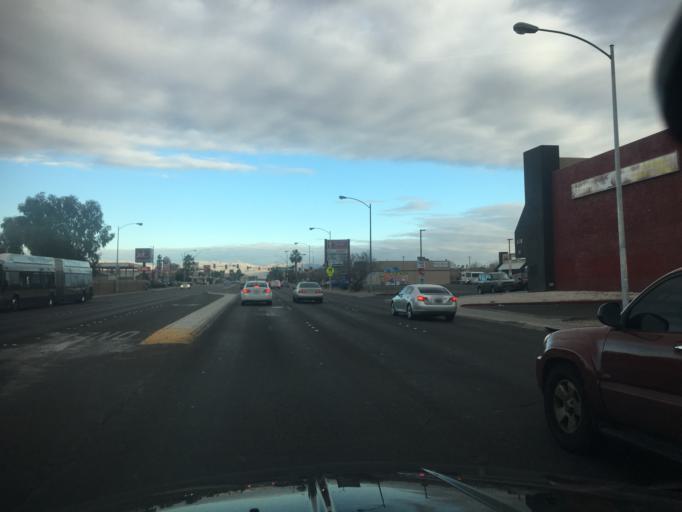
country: US
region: Nevada
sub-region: Clark County
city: Winchester
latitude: 36.1278
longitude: -115.0653
